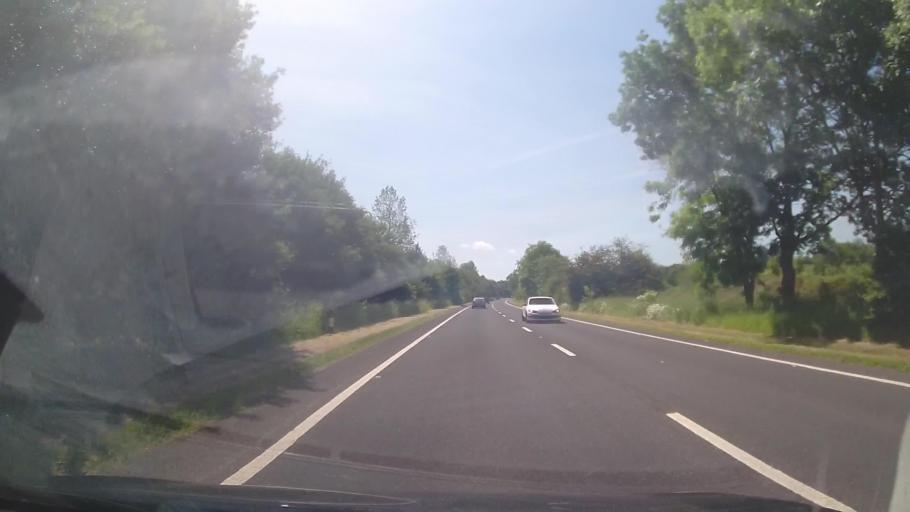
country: GB
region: England
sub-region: Herefordshire
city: Hope under Dinmore
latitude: 52.2017
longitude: -2.7196
